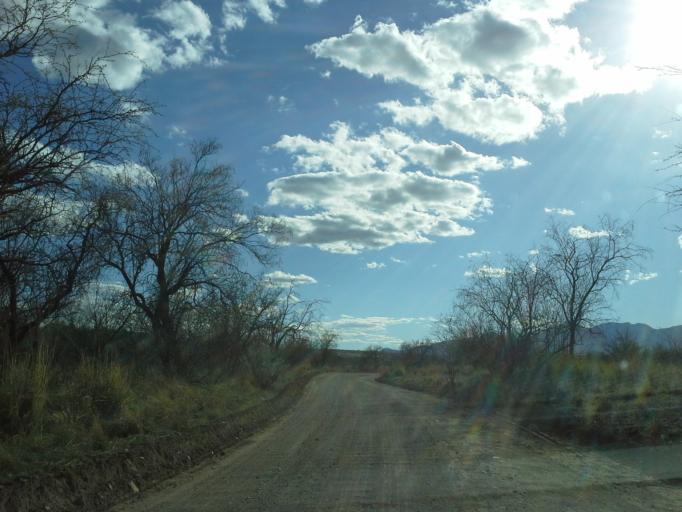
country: US
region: Arizona
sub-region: Pima County
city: Corona de Tucson
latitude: 31.7370
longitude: -110.6701
